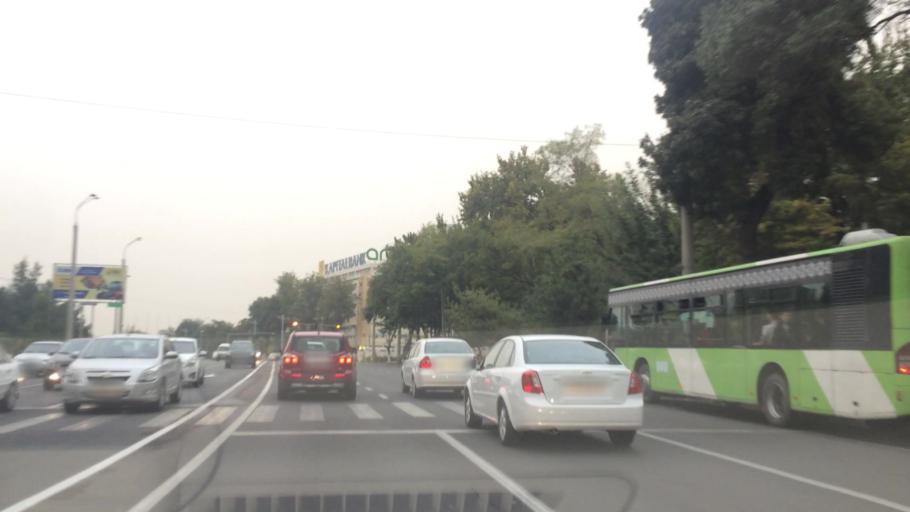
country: UZ
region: Toshkent Shahri
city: Tashkent
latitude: 41.3040
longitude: 69.2675
